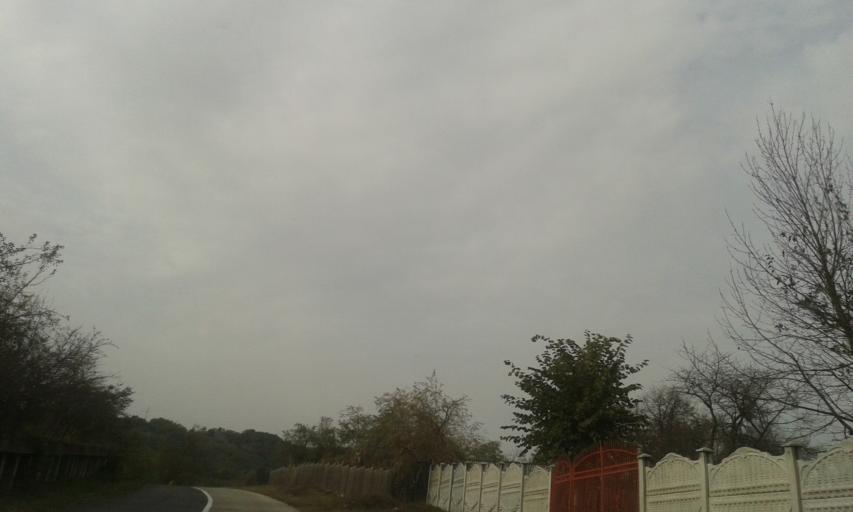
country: RO
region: Valcea
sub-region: Comuna Gradistea
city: Gradistea
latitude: 44.9166
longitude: 23.7794
